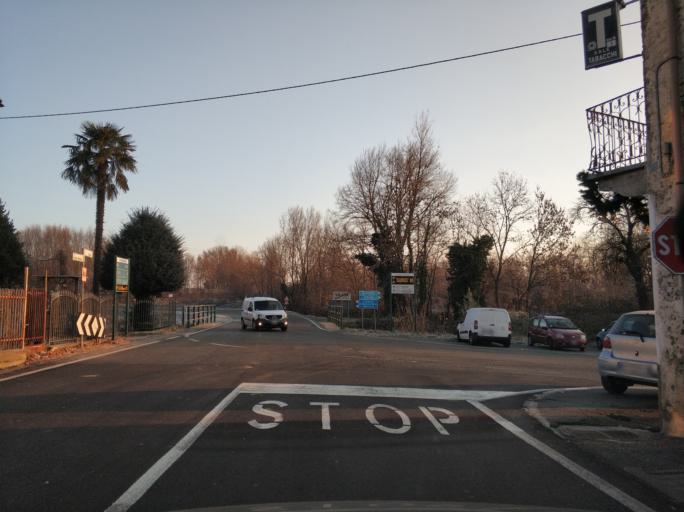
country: IT
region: Piedmont
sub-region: Provincia di Torino
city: Nole
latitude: 45.2578
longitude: 7.5820
